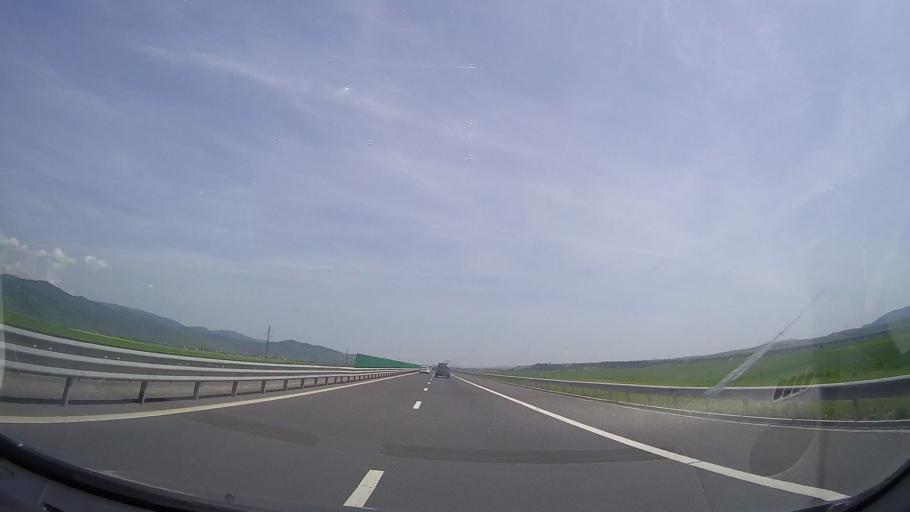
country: RO
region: Alba
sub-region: Comuna Sibot
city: Sibot
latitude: 45.9112
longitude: 23.3177
